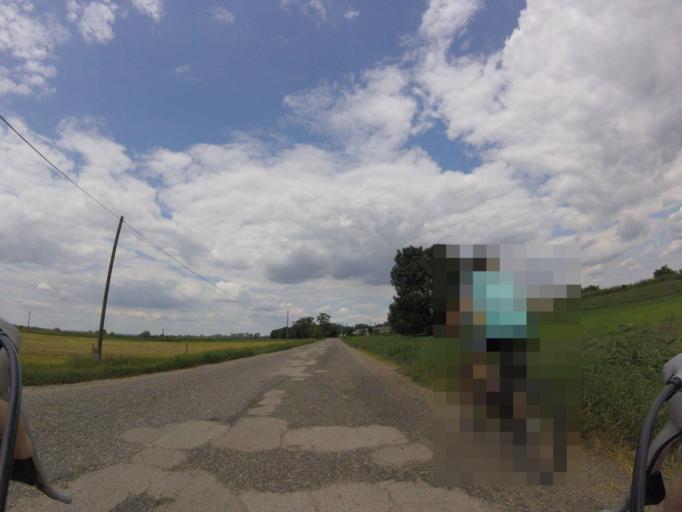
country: HU
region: Fejer
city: Seregelyes
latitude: 47.1404
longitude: 18.5752
